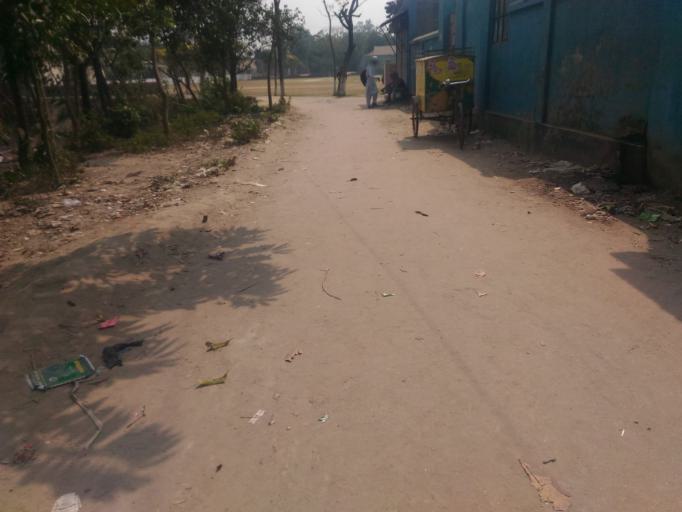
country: BD
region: Dhaka
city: Narayanganj
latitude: 23.6396
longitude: 90.4374
